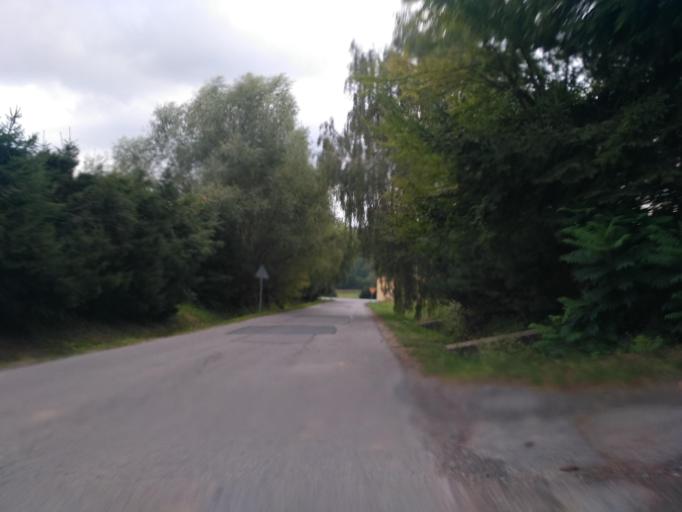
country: PL
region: Subcarpathian Voivodeship
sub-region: Powiat rzeszowski
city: Chmielnik
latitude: 49.9827
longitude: 22.1190
